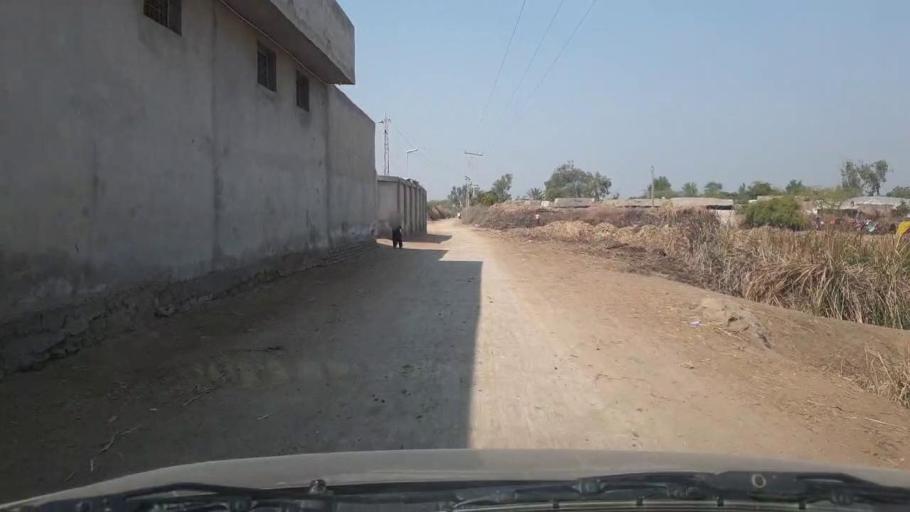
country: PK
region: Sindh
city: Mirwah Gorchani
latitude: 25.3553
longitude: 69.1465
